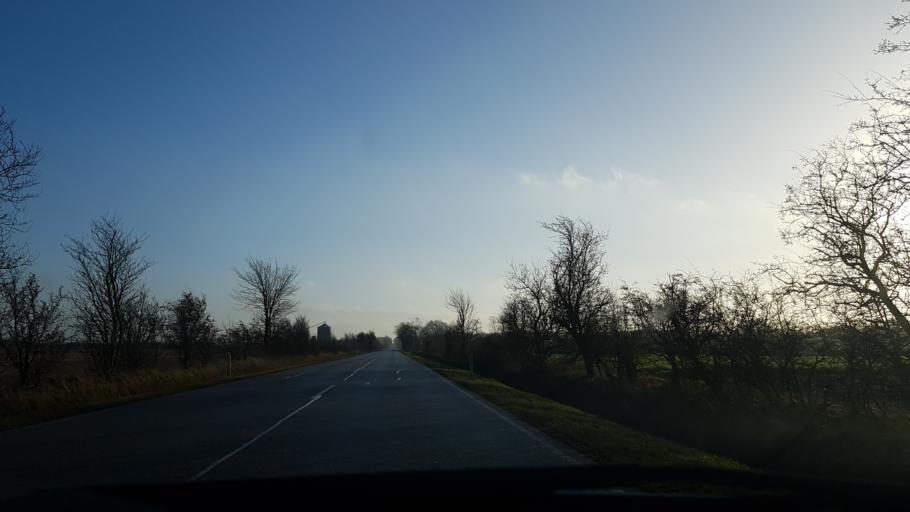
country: DK
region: South Denmark
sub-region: Tonder Kommune
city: Toftlund
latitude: 55.2341
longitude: 9.1657
